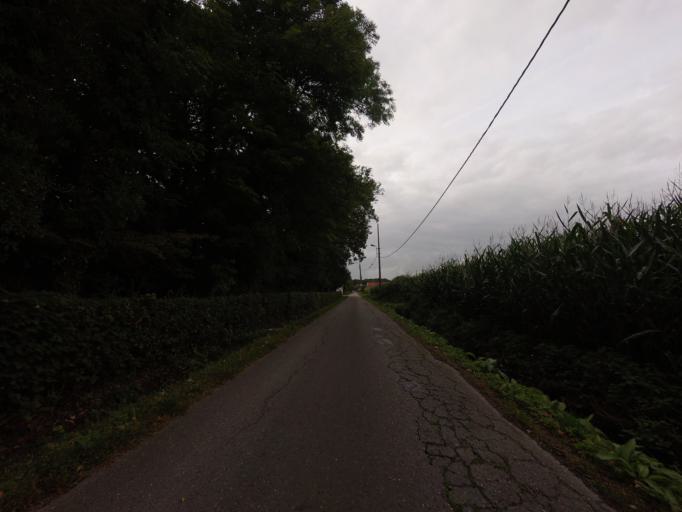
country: BE
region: Flanders
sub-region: Provincie Vlaams-Brabant
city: Meise
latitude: 50.9711
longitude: 4.3216
